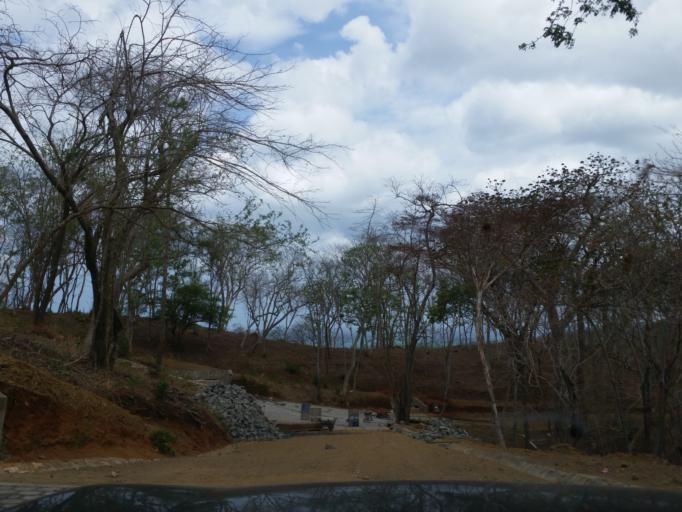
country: NI
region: Rivas
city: Tola
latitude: 11.4276
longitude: -86.0680
